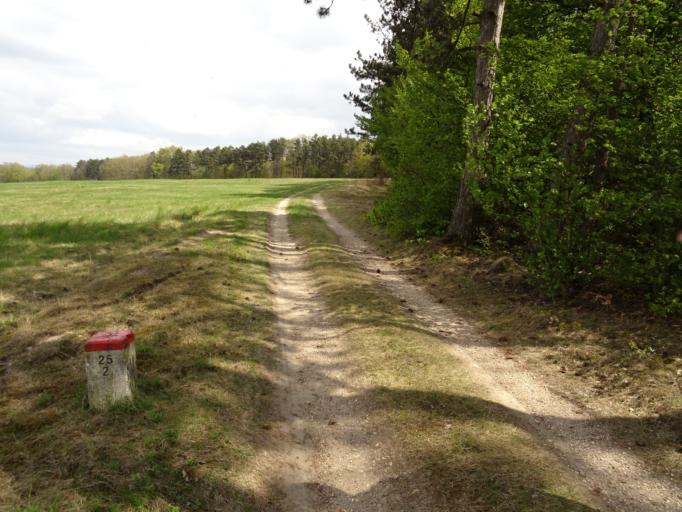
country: HU
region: Borsod-Abauj-Zemplen
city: Gonc
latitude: 48.5170
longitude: 21.1539
